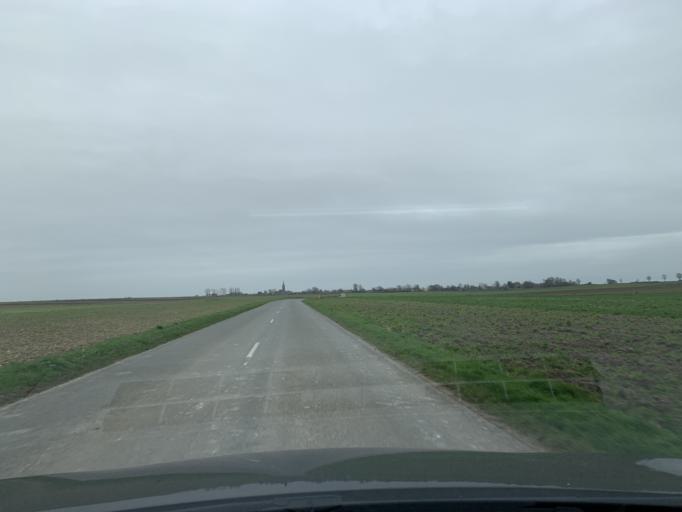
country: FR
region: Nord-Pas-de-Calais
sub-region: Departement du Pas-de-Calais
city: Oisy-le-Verger
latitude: 50.2395
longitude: 3.1486
